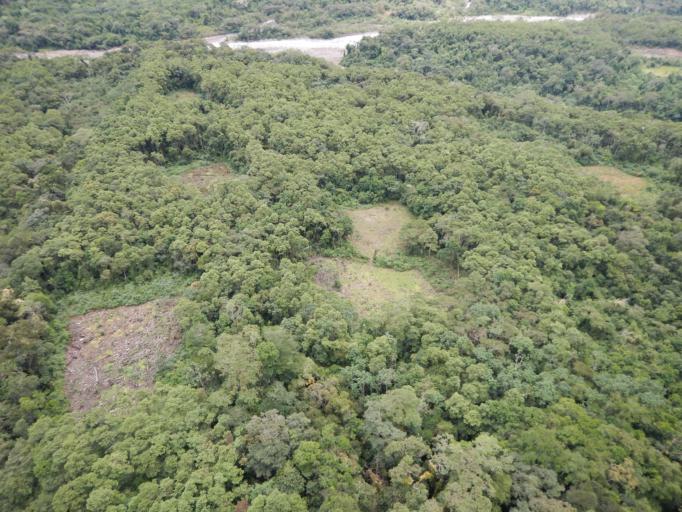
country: BO
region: Cochabamba
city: Totora
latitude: -17.4794
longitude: -65.0072
